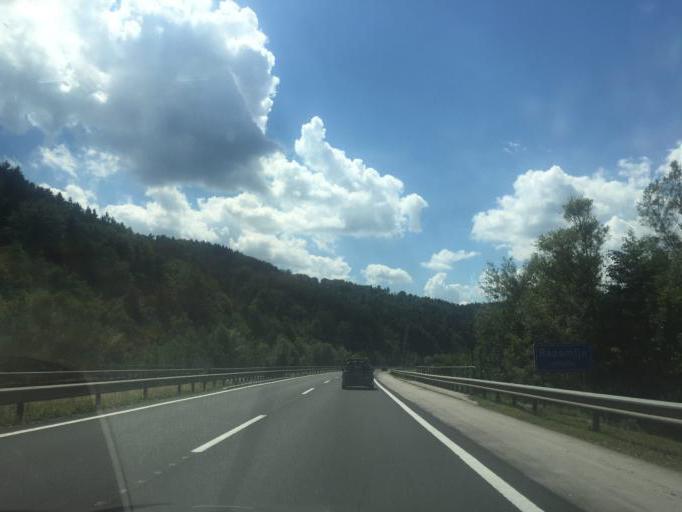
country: SI
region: Moravce
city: Moravce
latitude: 46.1639
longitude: 14.7536
